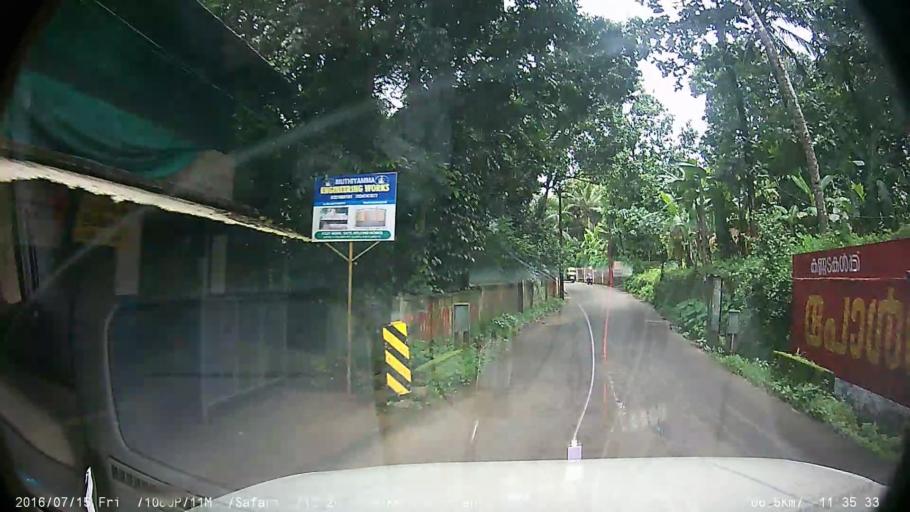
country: IN
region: Kerala
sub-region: Ernakulam
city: Piravam
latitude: 9.7762
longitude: 76.4973
